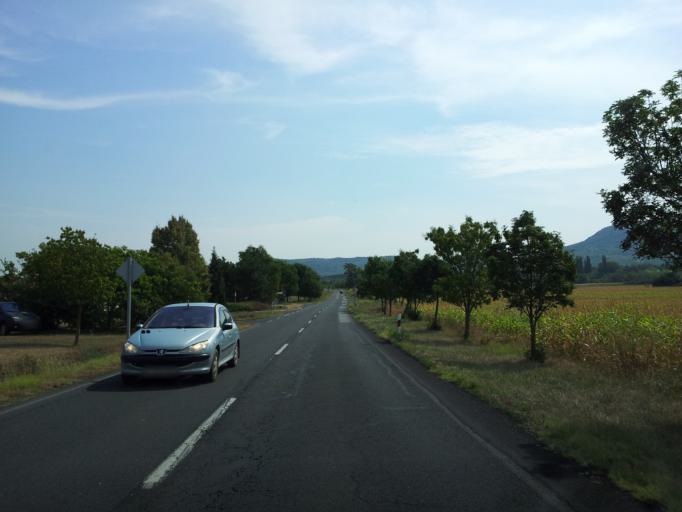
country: HU
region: Veszprem
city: Tapolca
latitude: 46.8832
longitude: 17.4705
